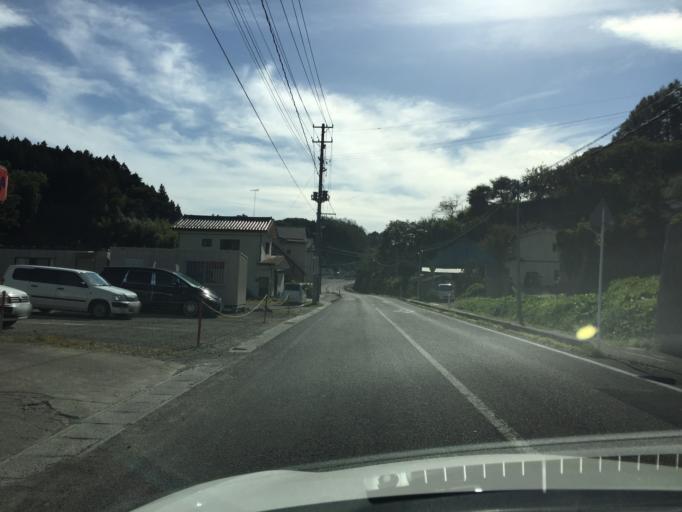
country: JP
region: Fukushima
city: Miharu
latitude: 37.4504
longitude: 140.4876
